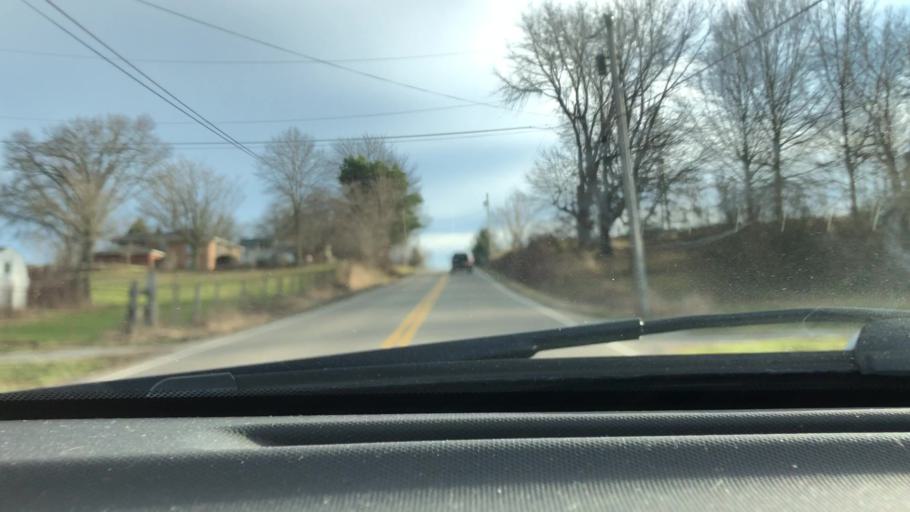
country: US
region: Ohio
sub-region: Wayne County
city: Dalton
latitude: 40.7949
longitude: -81.7455
